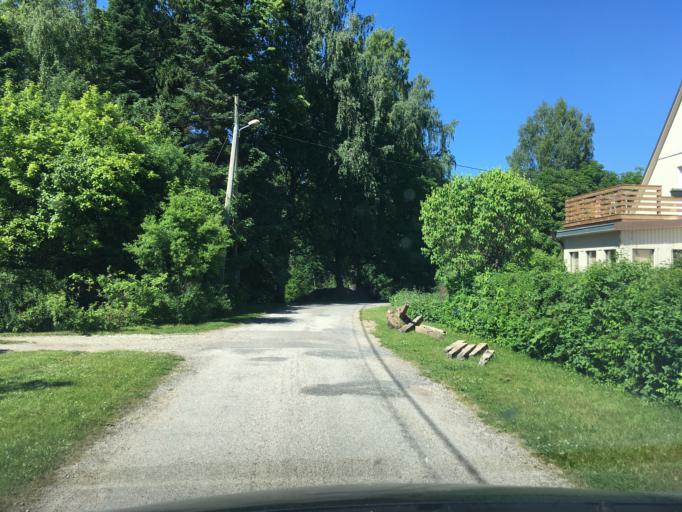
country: EE
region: Harju
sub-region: Raasiku vald
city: Raasiku
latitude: 59.1833
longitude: 25.1769
